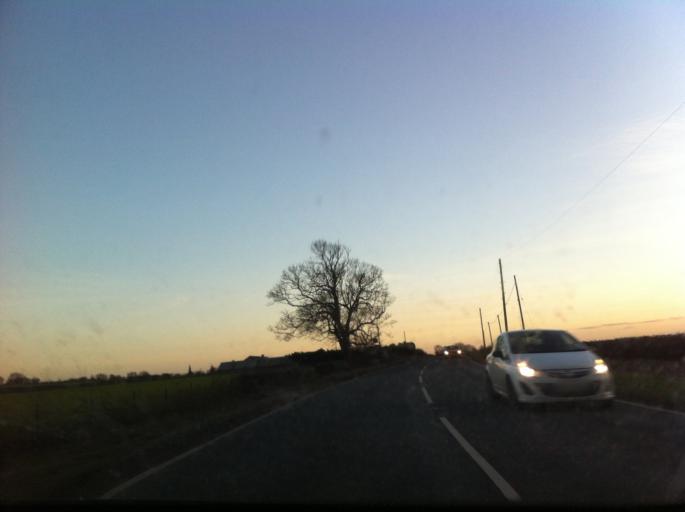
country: GB
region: England
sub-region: Northamptonshire
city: Irchester
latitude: 52.2715
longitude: -0.6759
